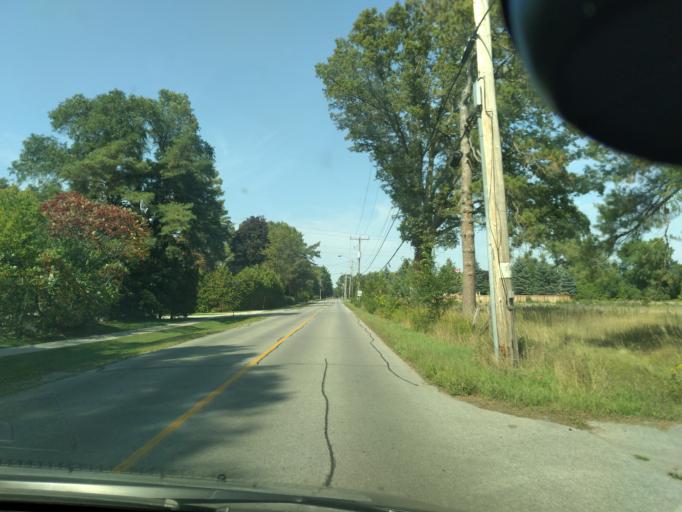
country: CA
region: Ontario
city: Newmarket
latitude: 44.1101
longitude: -79.5035
